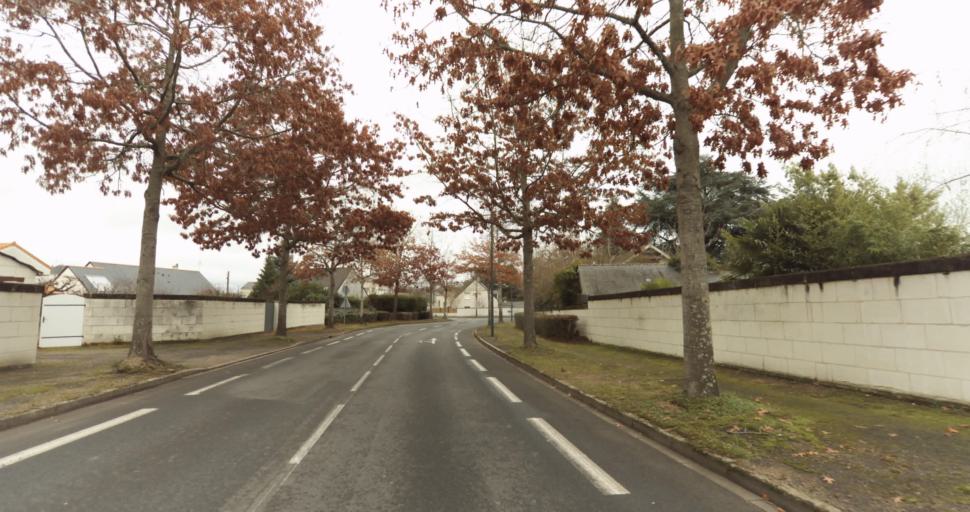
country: FR
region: Pays de la Loire
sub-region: Departement de Maine-et-Loire
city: Saumur
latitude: 47.2517
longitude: -0.0951
